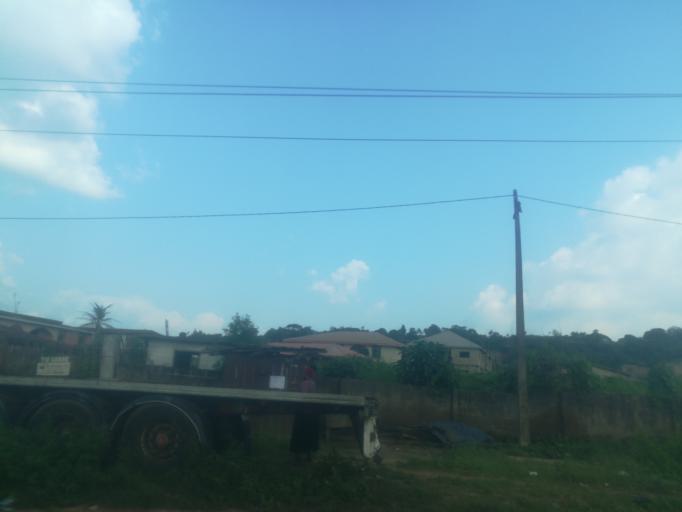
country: NG
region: Oyo
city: Moniya
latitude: 7.4868
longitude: 3.9145
